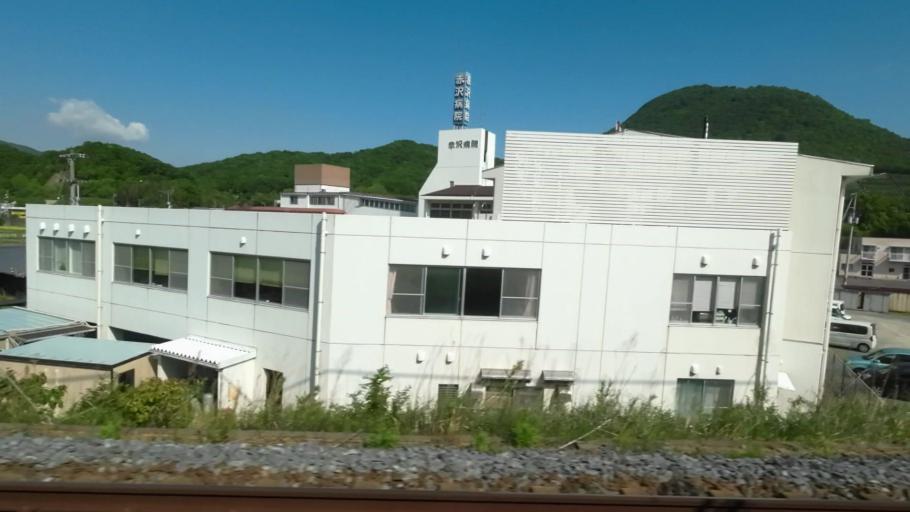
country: JP
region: Kagawa
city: Sakaidecho
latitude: 34.2944
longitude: 133.9368
